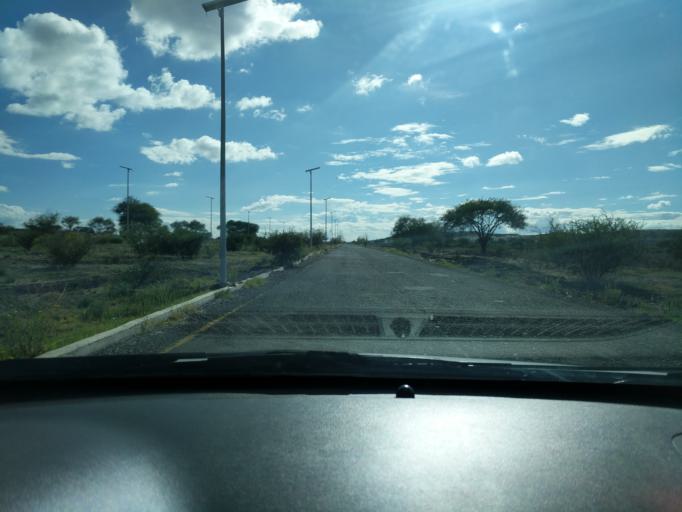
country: MX
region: Queretaro
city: La Canada
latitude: 20.5969
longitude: -100.2994
